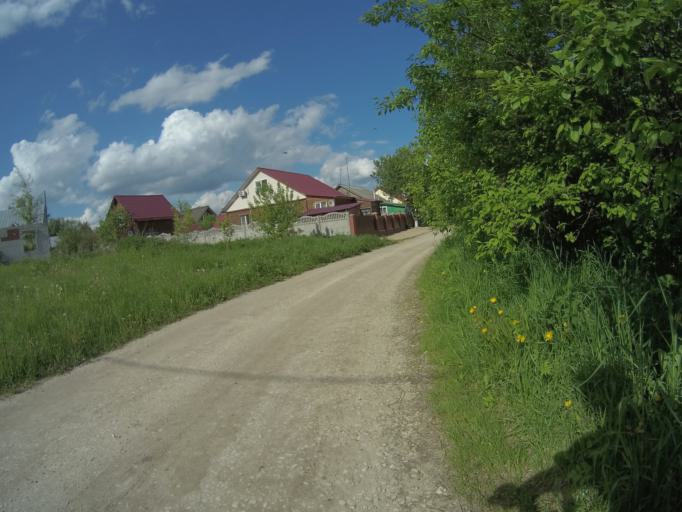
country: RU
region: Vladimir
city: Suzdal'
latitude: 56.4135
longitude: 40.4292
